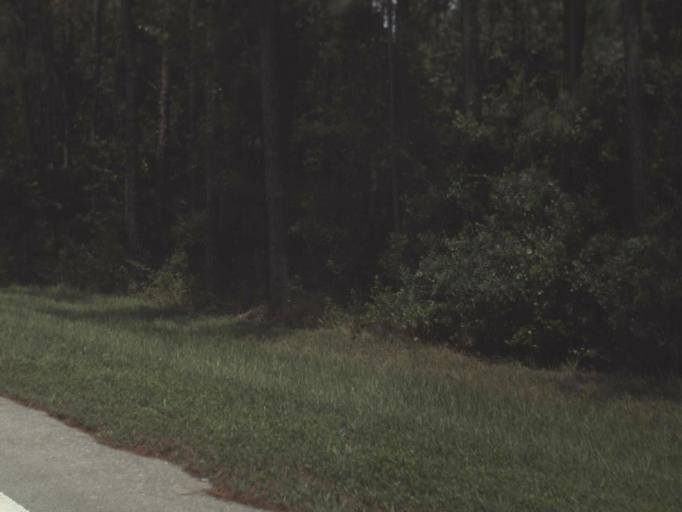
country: US
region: Florida
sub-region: Baker County
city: Macclenny
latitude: 30.1511
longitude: -82.1854
